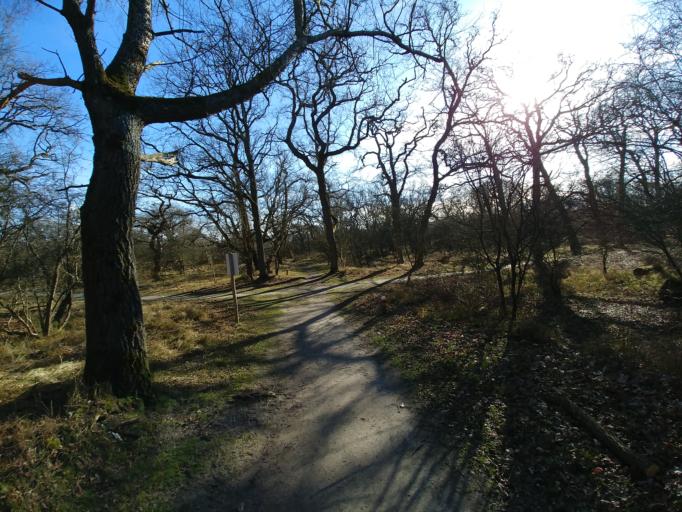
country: NL
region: South Holland
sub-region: Gemeente Leidschendam-Voorburg
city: Voorburg
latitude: 52.1272
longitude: 4.3328
